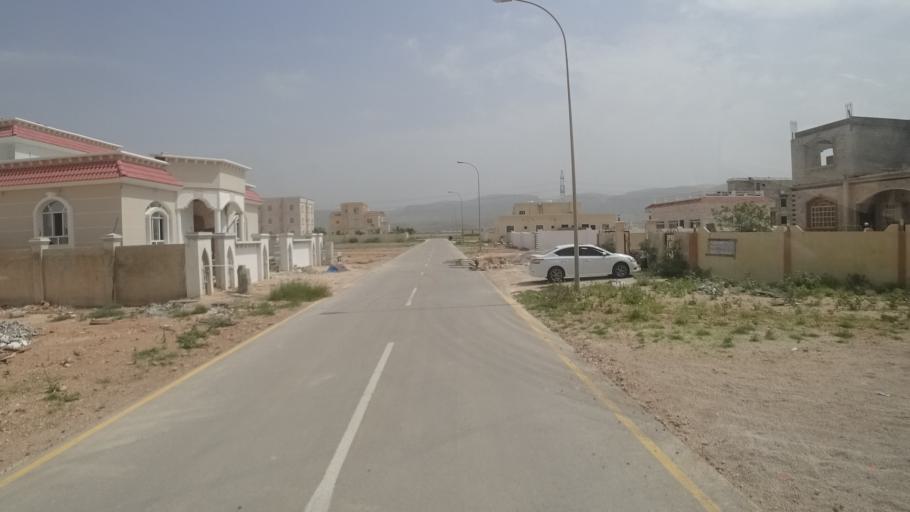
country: OM
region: Zufar
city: Salalah
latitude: 17.1007
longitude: 54.2145
